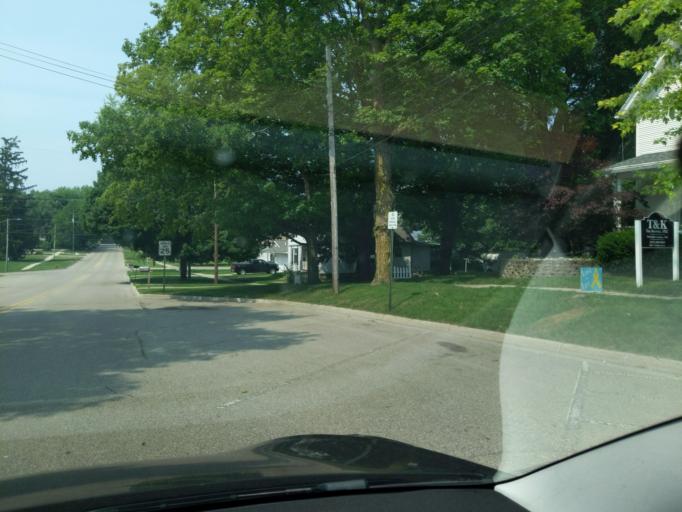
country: US
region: Michigan
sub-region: Clinton County
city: DeWitt
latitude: 42.8431
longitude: -84.5691
